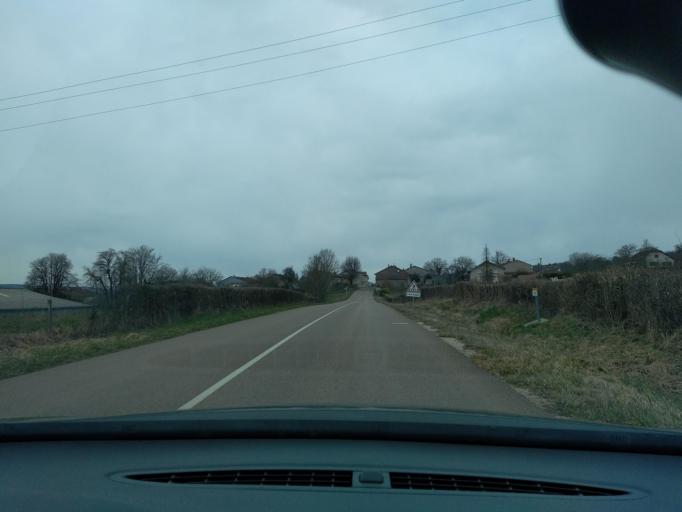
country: FR
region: Franche-Comte
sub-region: Departement du Jura
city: Arinthod
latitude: 46.3769
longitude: 5.5630
